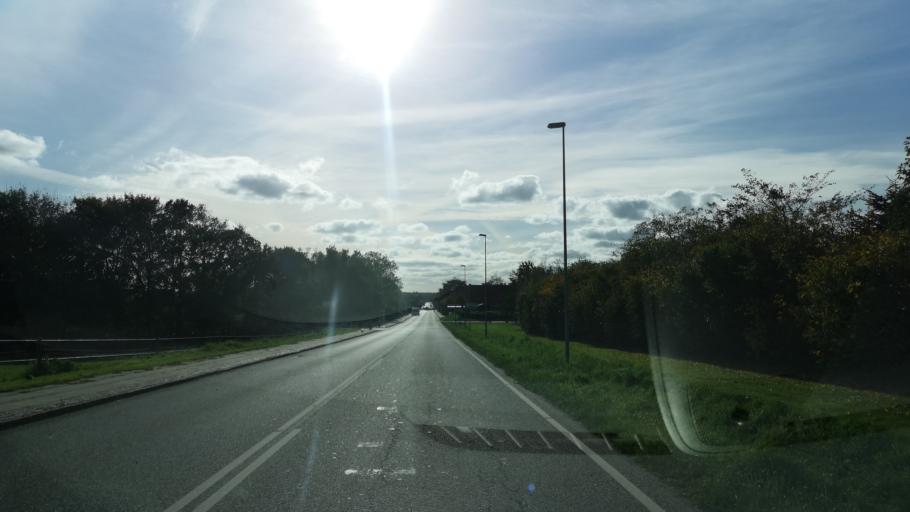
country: DK
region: Central Jutland
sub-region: Holstebro Kommune
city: Holstebro
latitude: 56.3738
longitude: 8.6358
